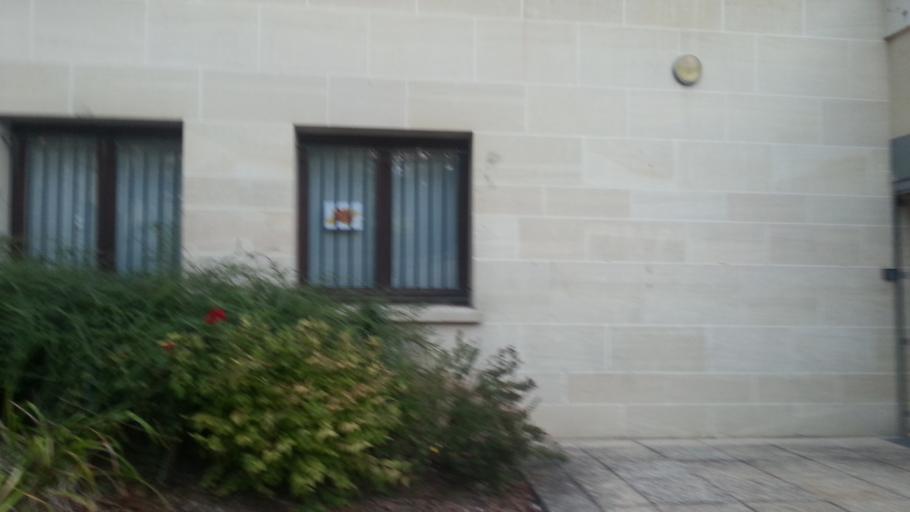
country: FR
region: Picardie
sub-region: Departement de l'Oise
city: Saint-Maximin
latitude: 49.2227
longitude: 2.4425
